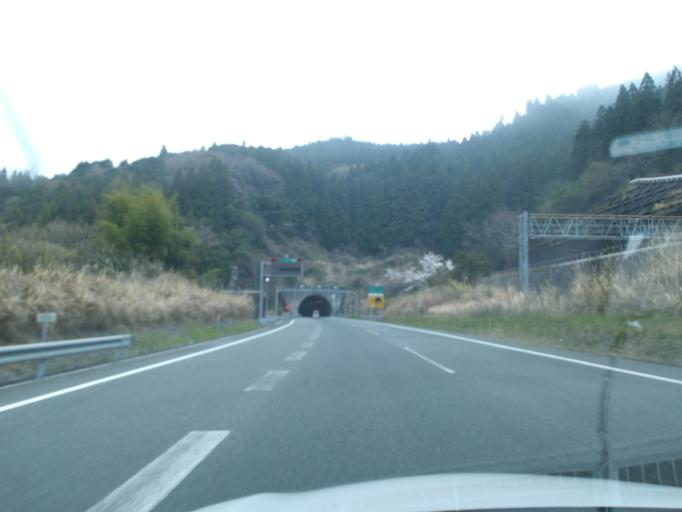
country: JP
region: Kochi
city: Kochi-shi
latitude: 33.7722
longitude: 133.6603
